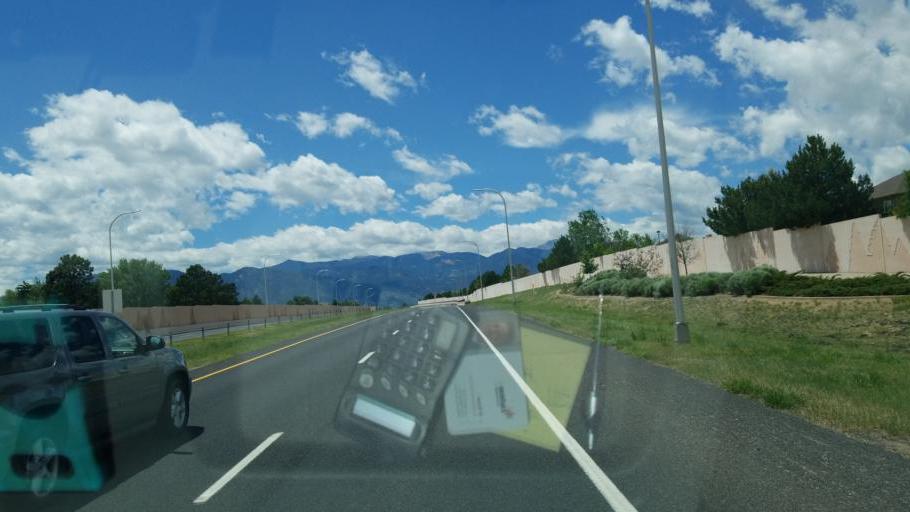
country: US
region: Colorado
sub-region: El Paso County
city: Security-Widefield
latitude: 38.7815
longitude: -104.7262
